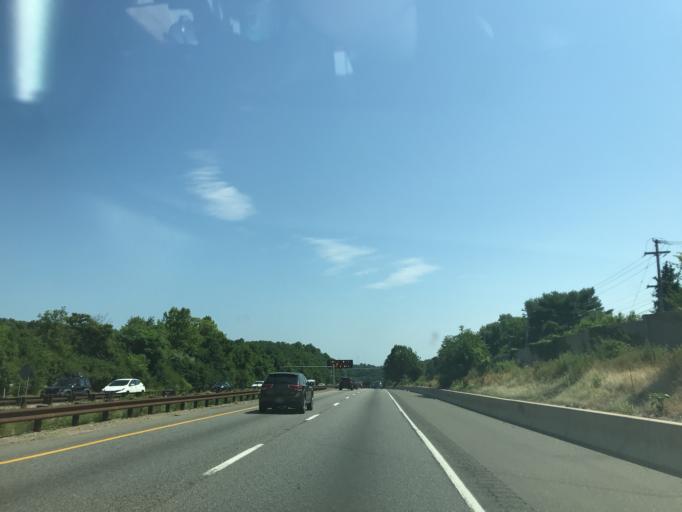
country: US
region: Pennsylvania
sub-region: Delaware County
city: Springfield
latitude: 39.9479
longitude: -75.3450
